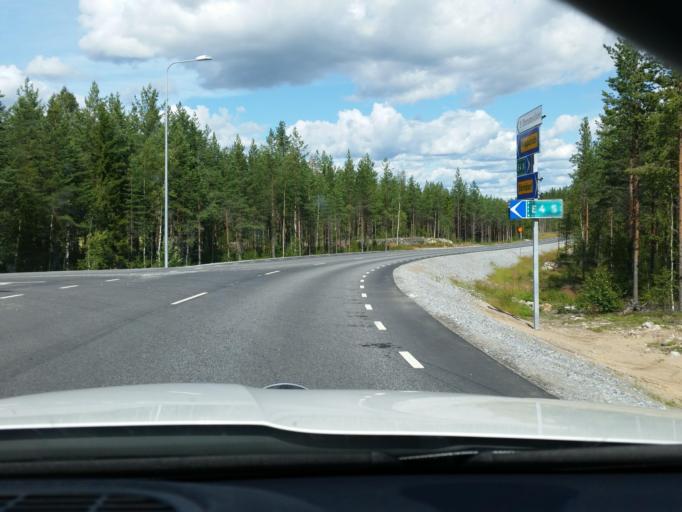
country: SE
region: Norrbotten
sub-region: Pitea Kommun
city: Norrfjarden
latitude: 65.3964
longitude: 21.4568
